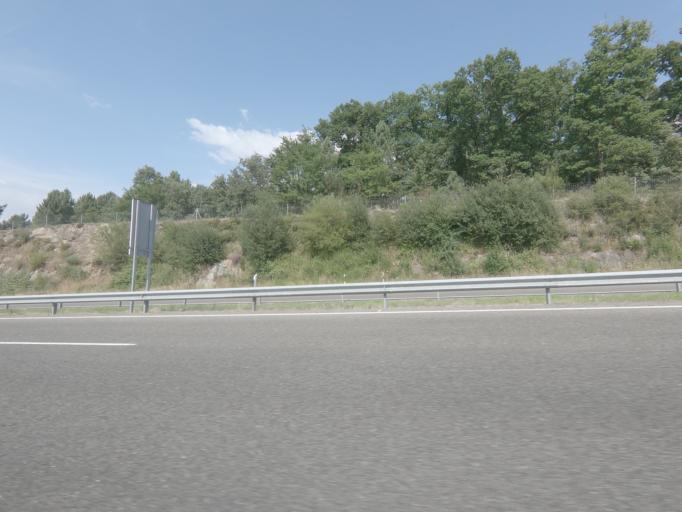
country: ES
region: Galicia
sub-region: Provincia de Ourense
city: Taboadela
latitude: 42.2729
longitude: -7.8721
